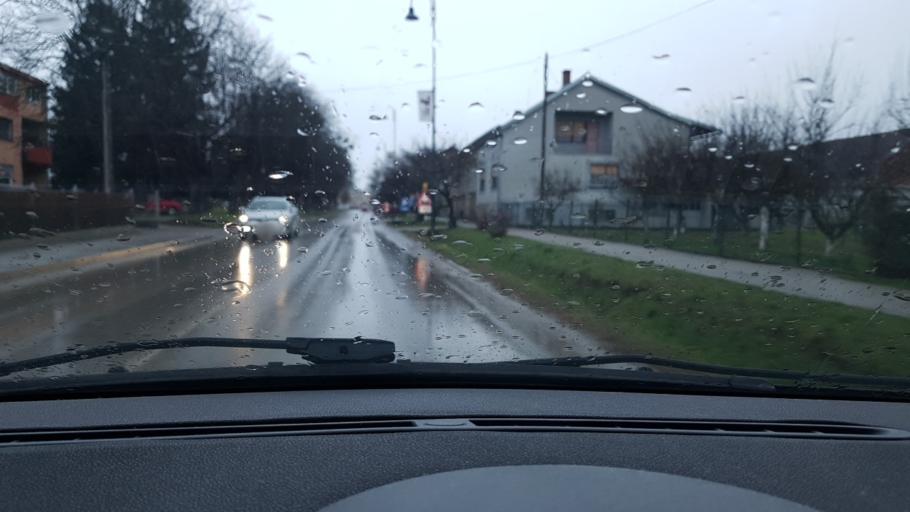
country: HR
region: Krapinsko-Zagorska
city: Oroslavje
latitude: 45.9810
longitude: 15.9644
